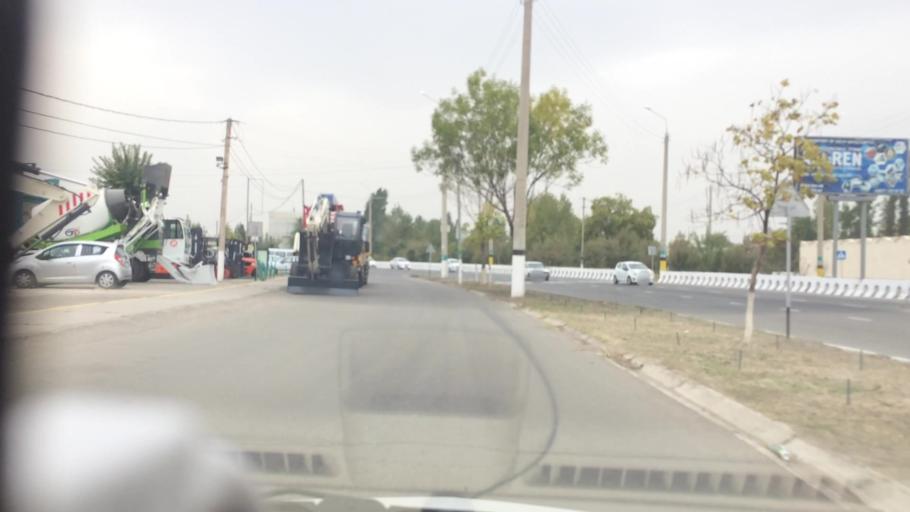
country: UZ
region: Toshkent
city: Salor
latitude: 41.3100
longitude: 69.3446
